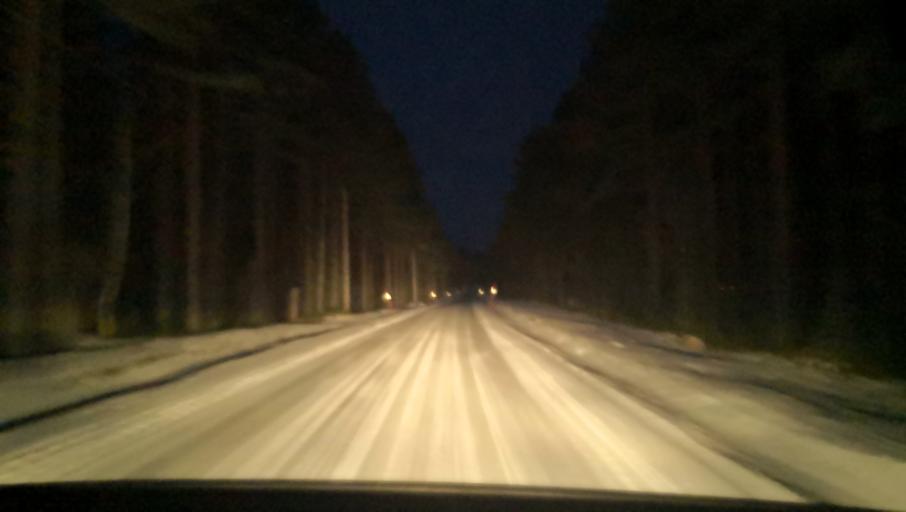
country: SE
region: Uppsala
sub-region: Heby Kommun
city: Tarnsjo
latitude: 60.2894
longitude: 16.8063
